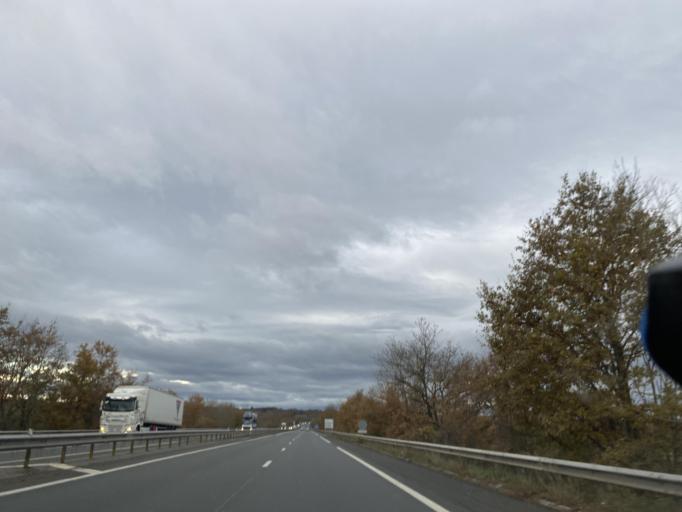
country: FR
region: Auvergne
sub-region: Departement du Puy-de-Dome
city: Peschadoires
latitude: 45.8603
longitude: 3.4942
